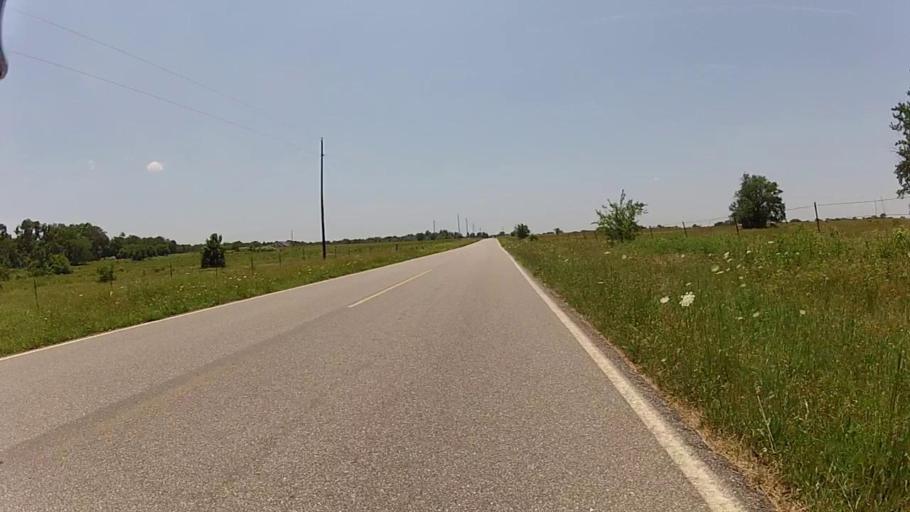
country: US
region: Kansas
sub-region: Montgomery County
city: Cherryvale
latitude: 37.2281
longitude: -95.5379
